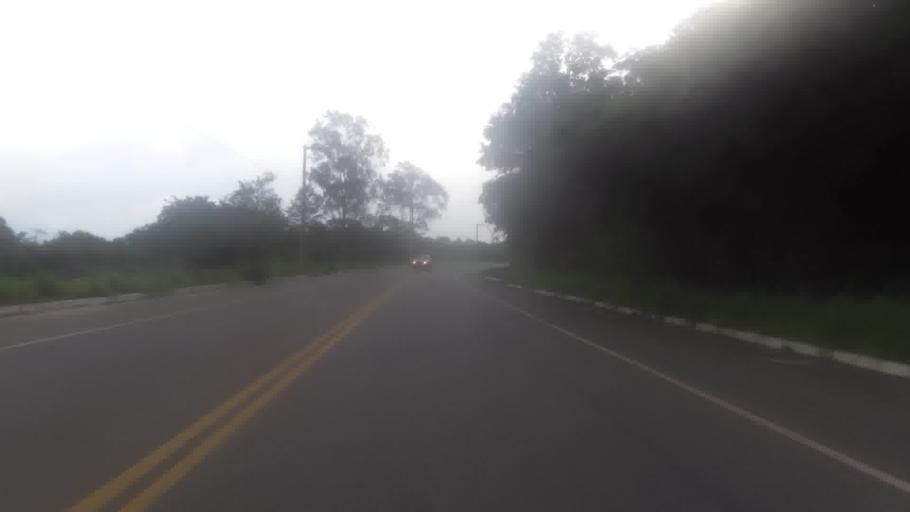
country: BR
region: Espirito Santo
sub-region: Piuma
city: Piuma
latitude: -20.8002
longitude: -40.6269
